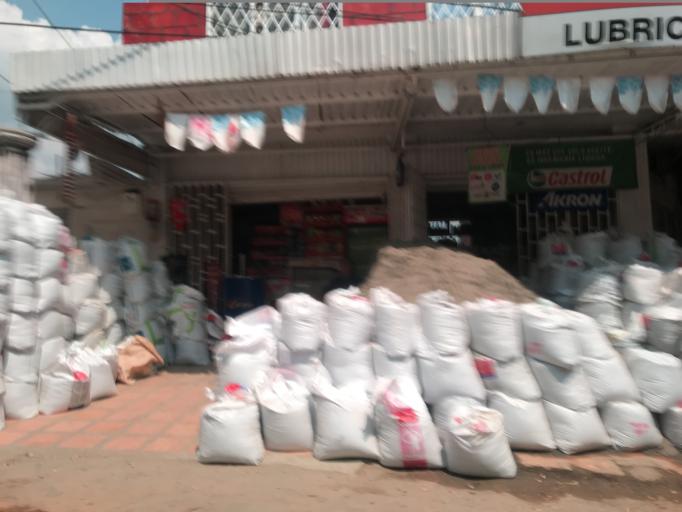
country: CO
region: Valle del Cauca
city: Cali
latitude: 3.4537
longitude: -76.5736
